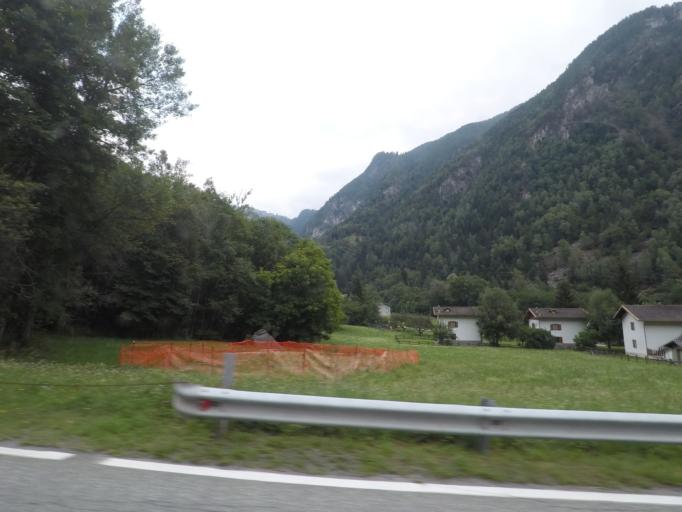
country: IT
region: Aosta Valley
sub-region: Valle d'Aosta
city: Antey-Saint-Andre
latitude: 45.8223
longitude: 7.5896
